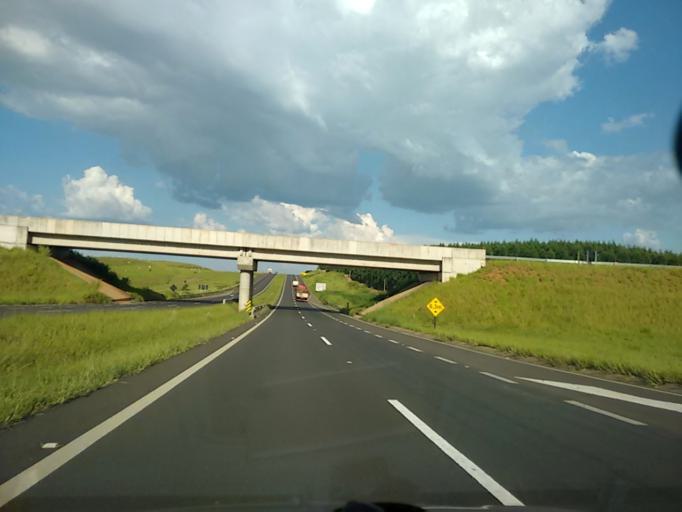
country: BR
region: Sao Paulo
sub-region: Duartina
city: Duartina
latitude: -22.3246
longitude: -49.4138
